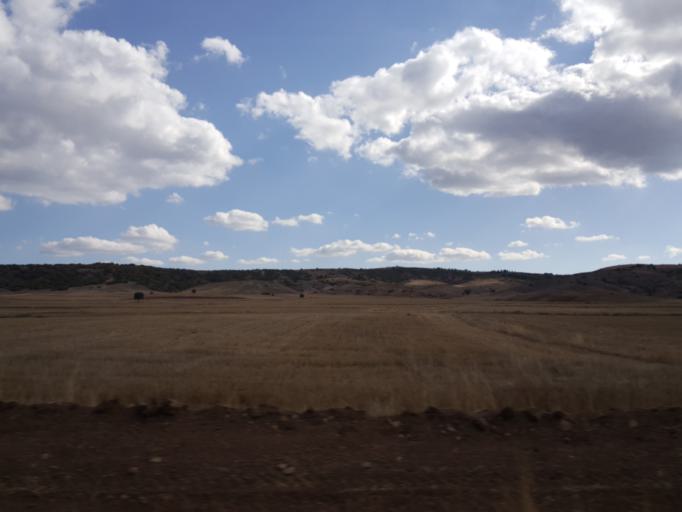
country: TR
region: Tokat
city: Sulusaray
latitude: 39.9867
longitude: 35.9676
